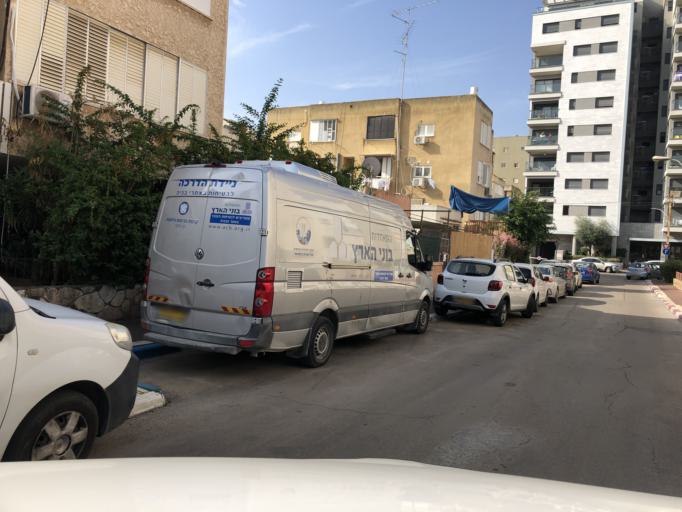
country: IL
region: Tel Aviv
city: Bene Beraq
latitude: 32.0680
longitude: 34.8307
